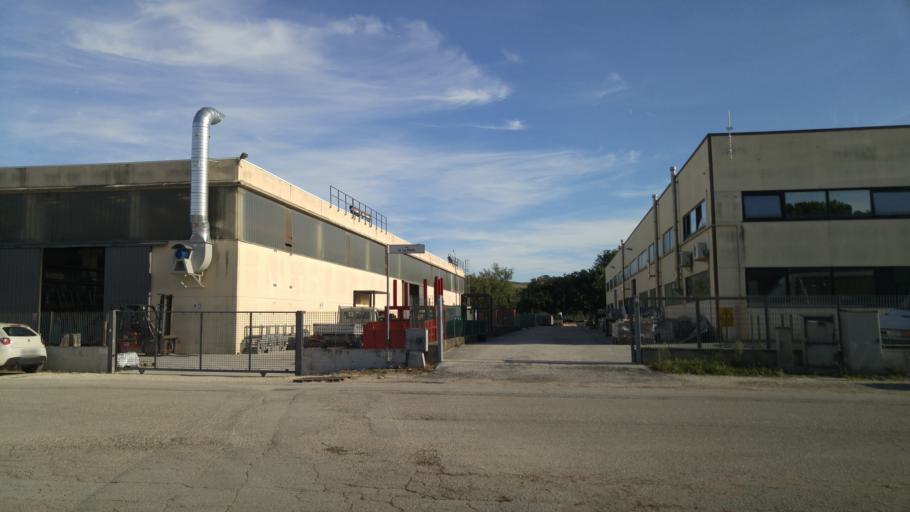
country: IT
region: The Marches
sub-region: Provincia di Pesaro e Urbino
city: Bellocchi
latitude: 43.7849
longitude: 13.0067
